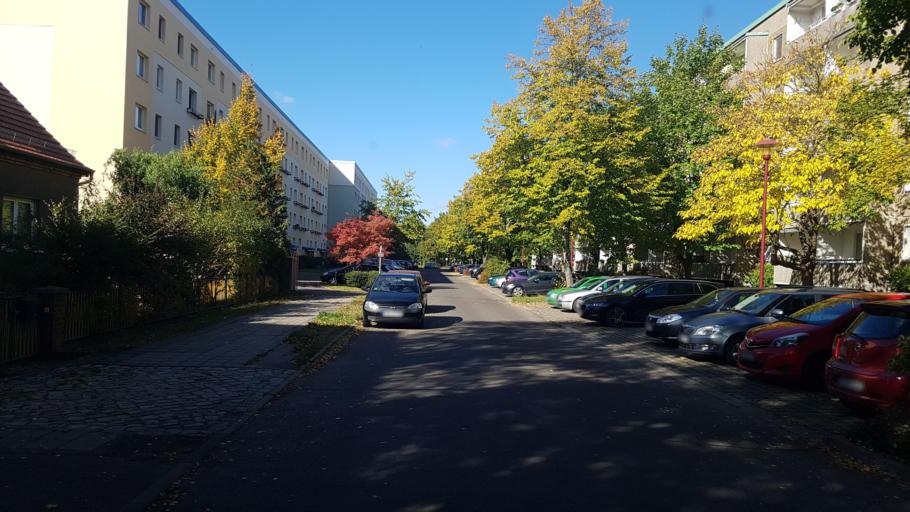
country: DE
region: Brandenburg
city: Cottbus
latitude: 51.7573
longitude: 14.3036
